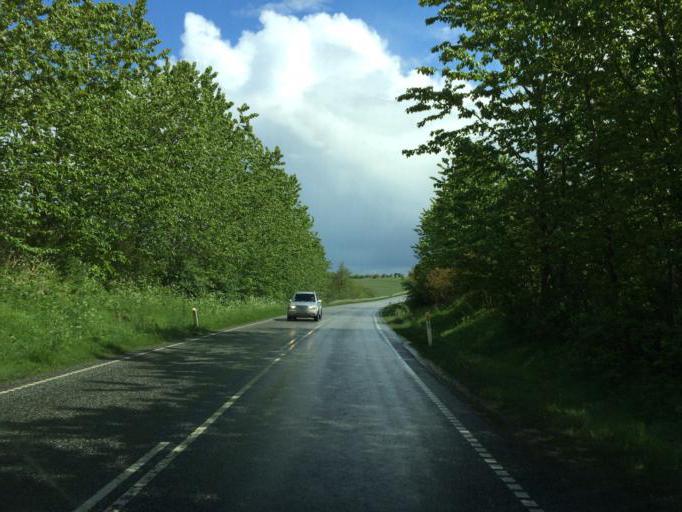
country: DK
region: Central Jutland
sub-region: Holstebro Kommune
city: Vinderup
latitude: 56.4441
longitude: 8.7257
